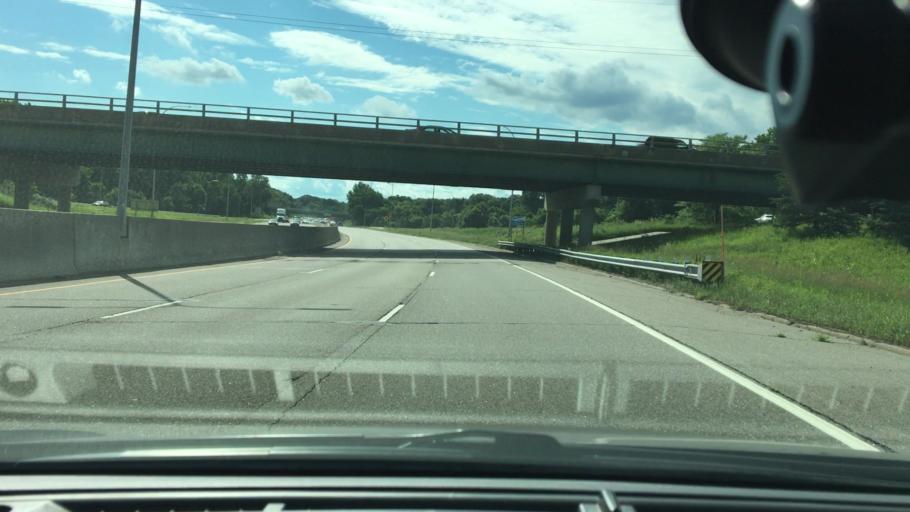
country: US
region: Minnesota
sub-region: Hennepin County
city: Wayzata
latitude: 44.9760
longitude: -93.5014
